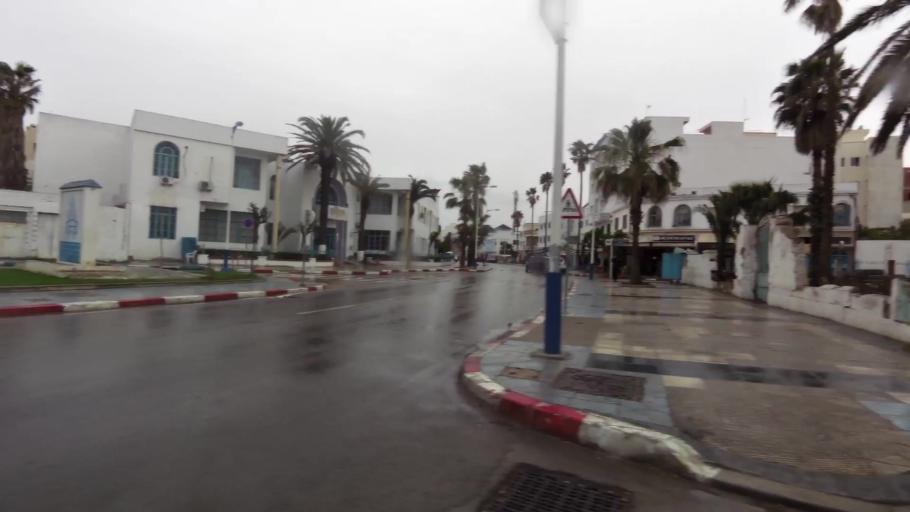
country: MA
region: Tanger-Tetouan
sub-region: Tetouan
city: Martil
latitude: 35.6176
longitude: -5.2764
